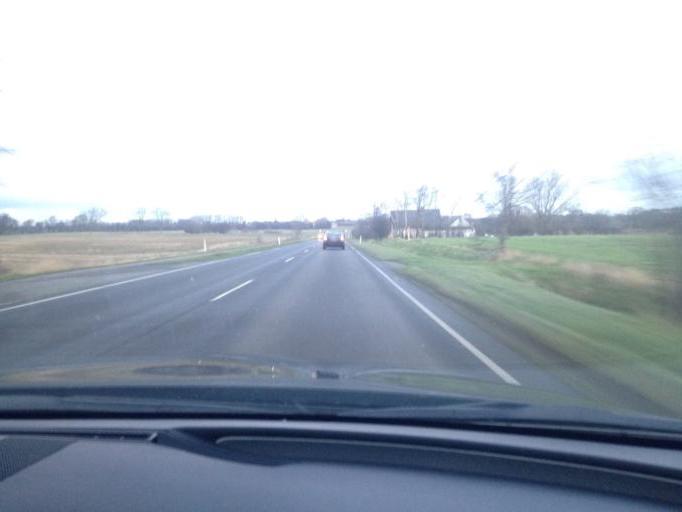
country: DK
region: South Denmark
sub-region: Kolding Kommune
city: Kolding
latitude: 55.5516
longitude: 9.4817
